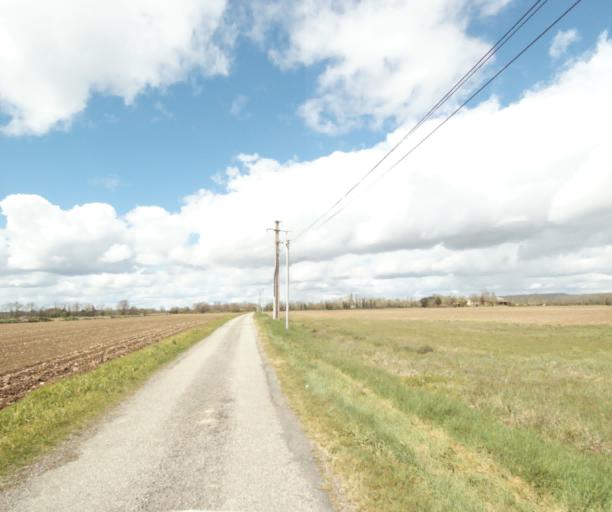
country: FR
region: Midi-Pyrenees
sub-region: Departement de l'Ariege
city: Saverdun
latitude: 43.2557
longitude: 1.5995
